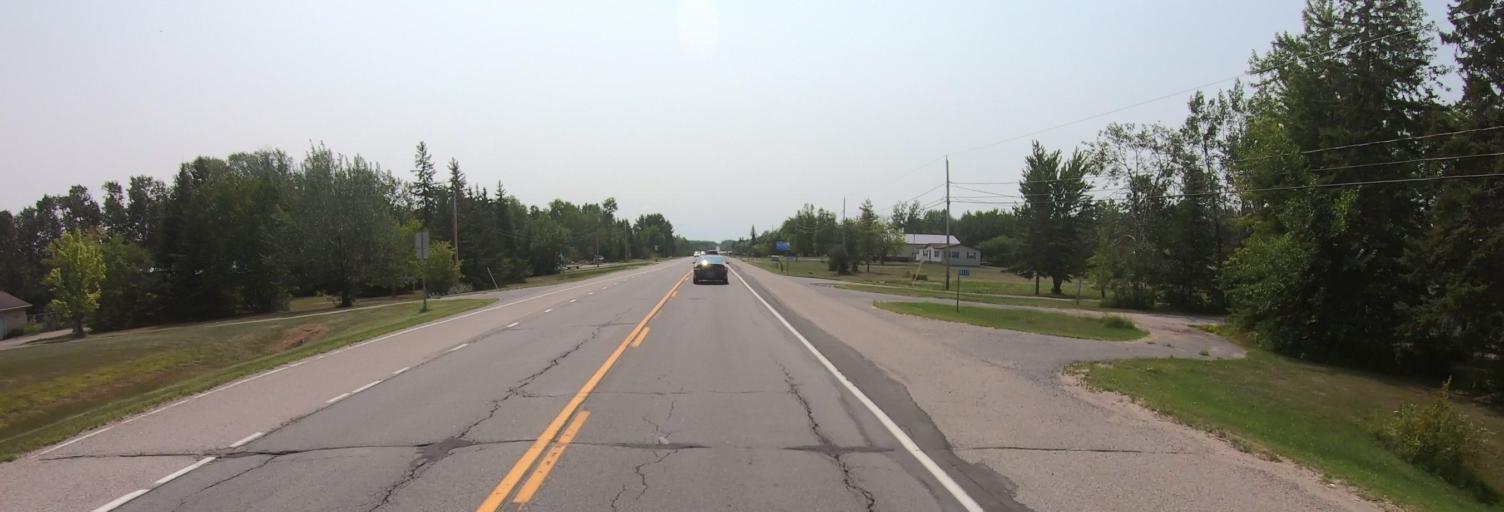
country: US
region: Minnesota
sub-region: Koochiching County
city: International Falls
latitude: 48.5692
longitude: -93.4400
